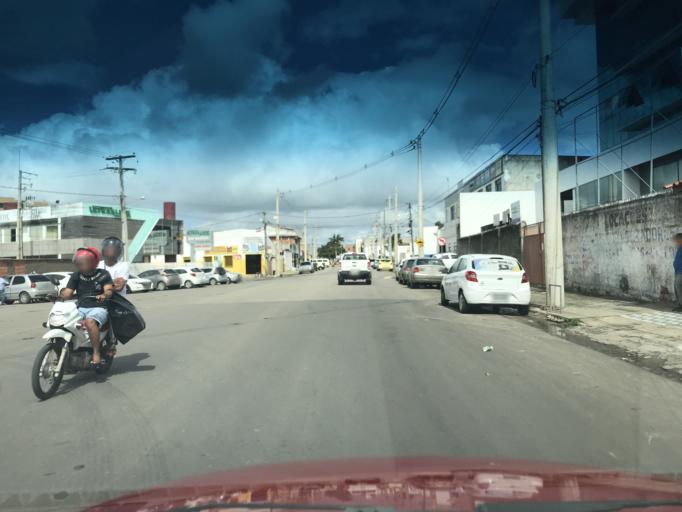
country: BR
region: Bahia
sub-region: Santo Antonio De Jesus
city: Santo Antonio de Jesus
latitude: -12.9671
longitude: -39.2700
